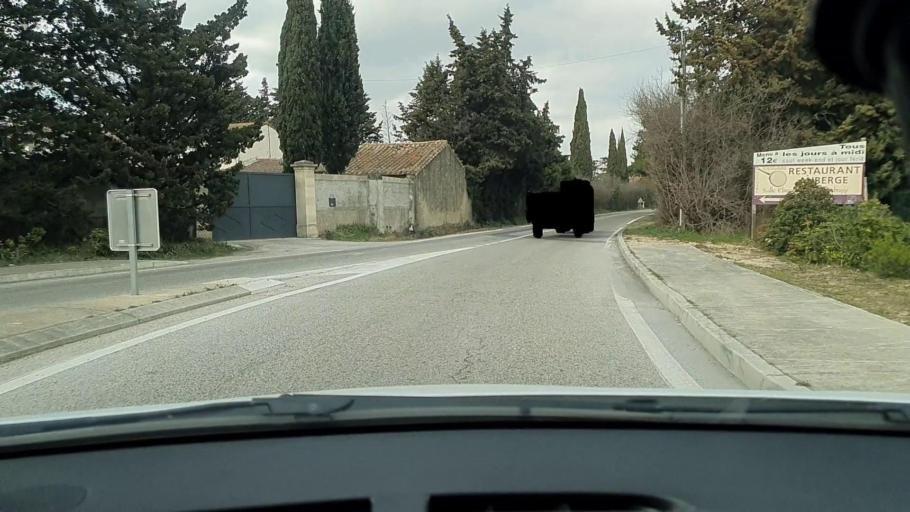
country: FR
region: Languedoc-Roussillon
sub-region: Departement du Gard
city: Sernhac
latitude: 43.9139
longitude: 4.5660
